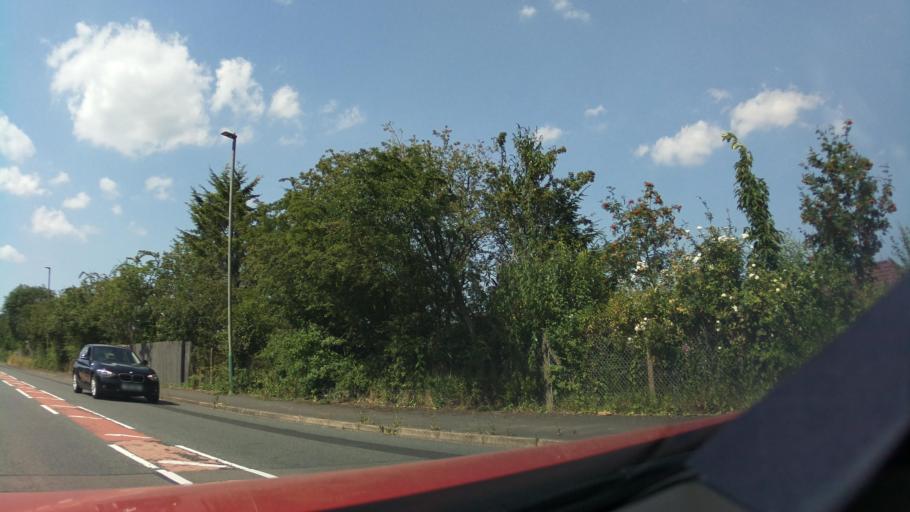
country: GB
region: Wales
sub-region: Caerphilly County Borough
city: Rhymney
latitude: 51.7405
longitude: -3.2748
